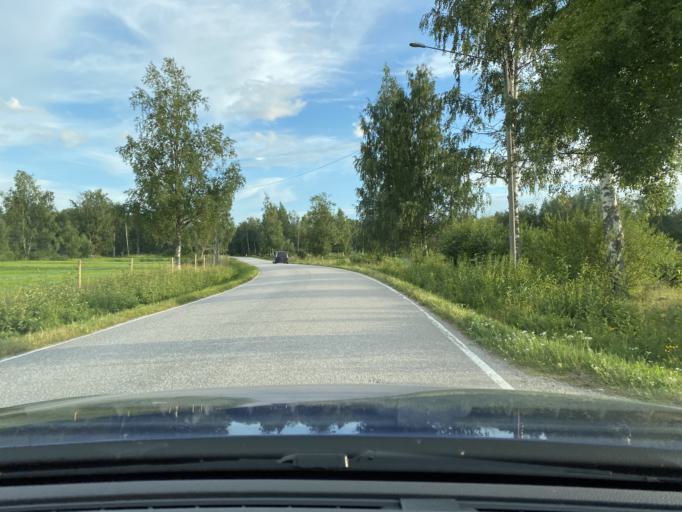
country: FI
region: Ostrobothnia
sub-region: Vaasa
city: Korsnaes
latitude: 62.9628
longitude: 21.1890
